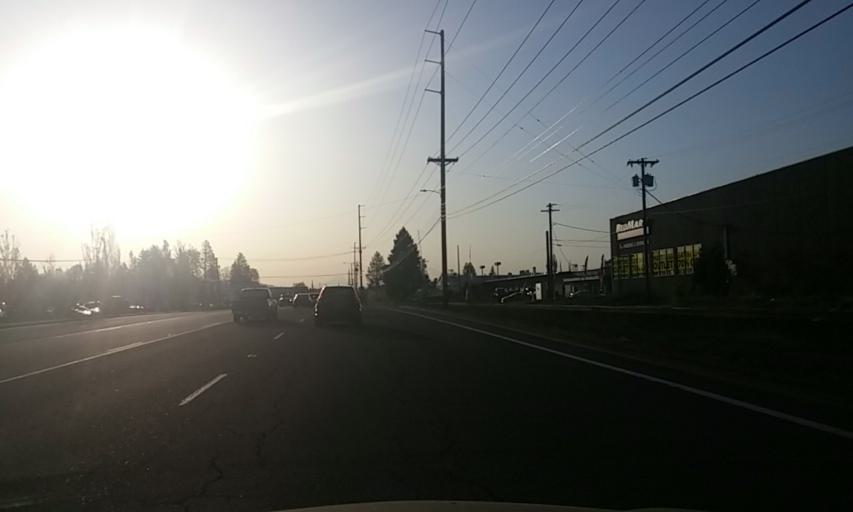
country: US
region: Oregon
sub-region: Washington County
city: Beaverton
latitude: 45.4892
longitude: -122.8236
